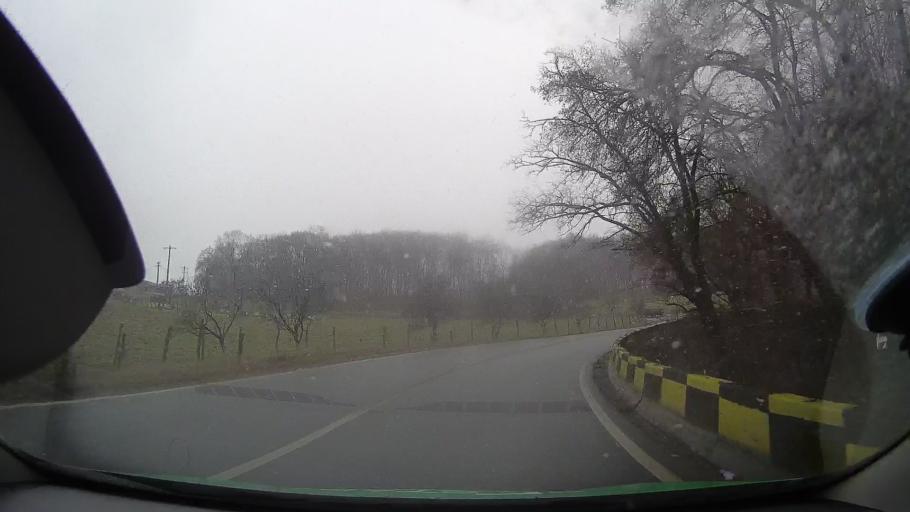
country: RO
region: Sibiu
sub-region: Municipiul Medias
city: Medias
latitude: 46.1851
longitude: 24.3251
